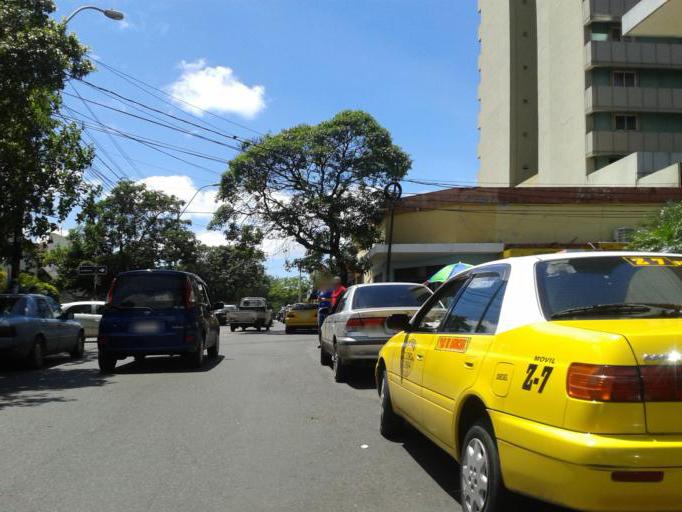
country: PY
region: Asuncion
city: Asuncion
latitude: -25.2911
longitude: -57.6254
